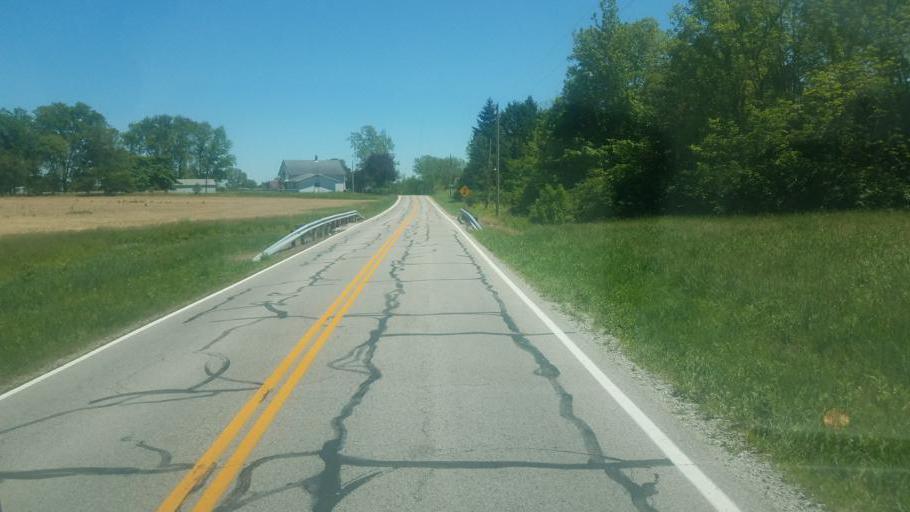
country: US
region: Ohio
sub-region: Miami County
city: Piqua
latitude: 40.2101
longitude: -84.2796
